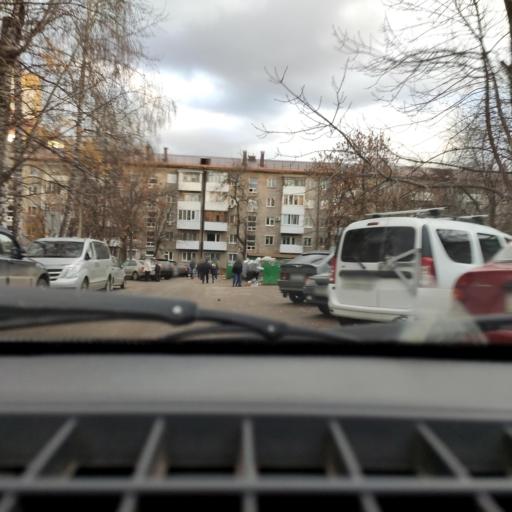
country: RU
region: Bashkortostan
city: Ufa
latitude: 54.7551
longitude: 55.9949
